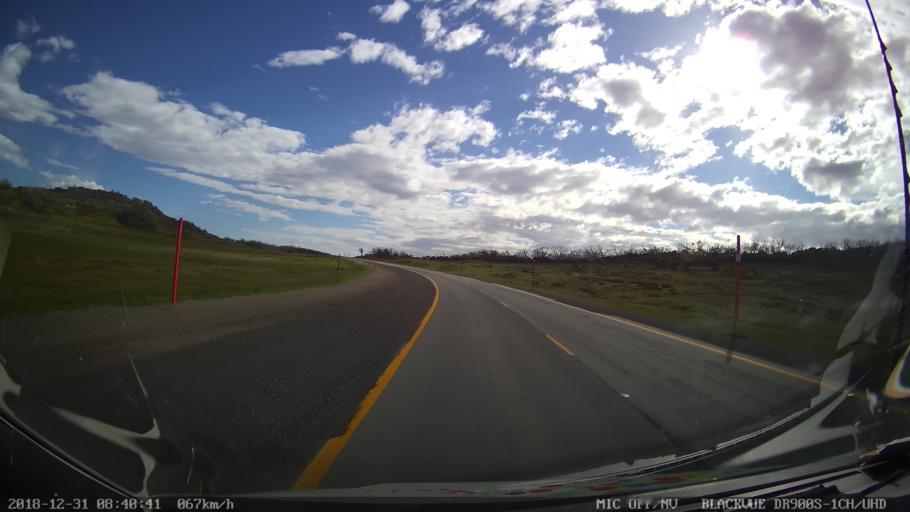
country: AU
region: New South Wales
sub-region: Snowy River
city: Jindabyne
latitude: -36.4038
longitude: 148.4156
